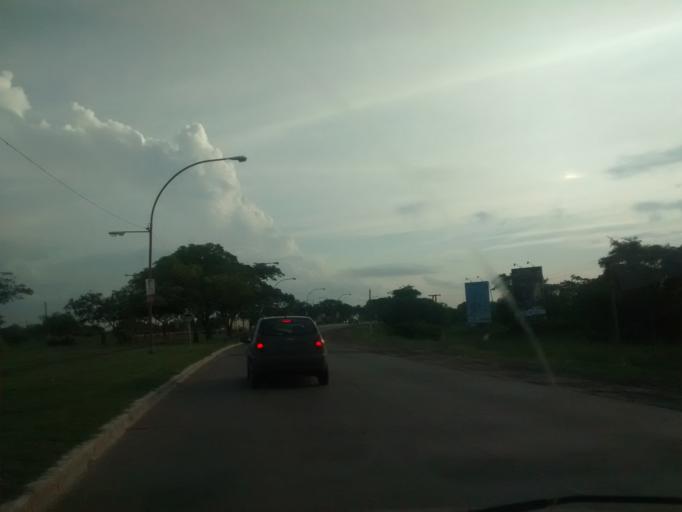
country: AR
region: Chaco
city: Resistencia
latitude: -27.4267
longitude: -58.9602
